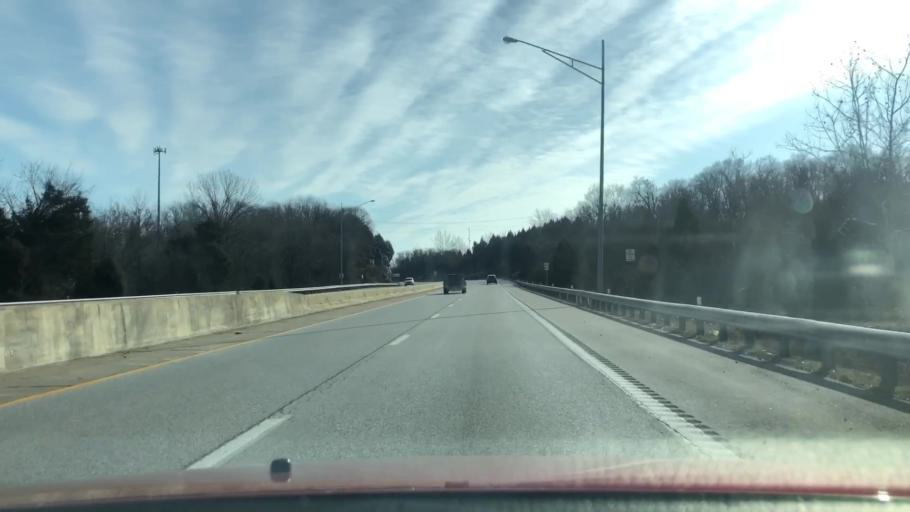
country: US
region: Missouri
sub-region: Christian County
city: Ozark
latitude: 37.1233
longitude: -93.2246
